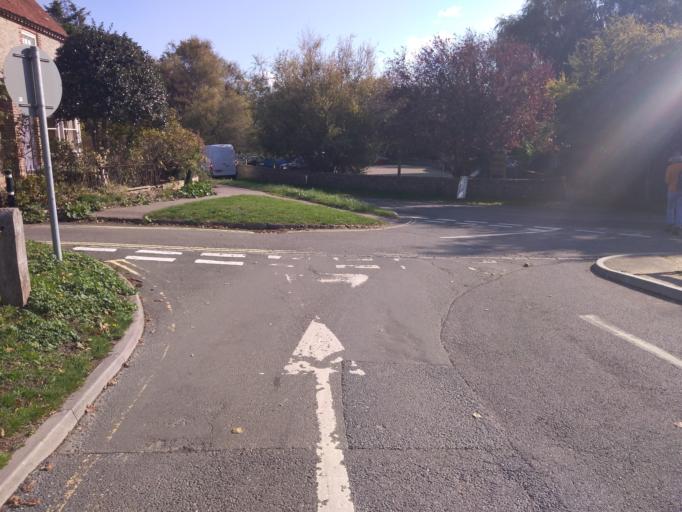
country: GB
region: England
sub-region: East Sussex
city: Seaford
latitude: 50.8093
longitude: 0.1568
